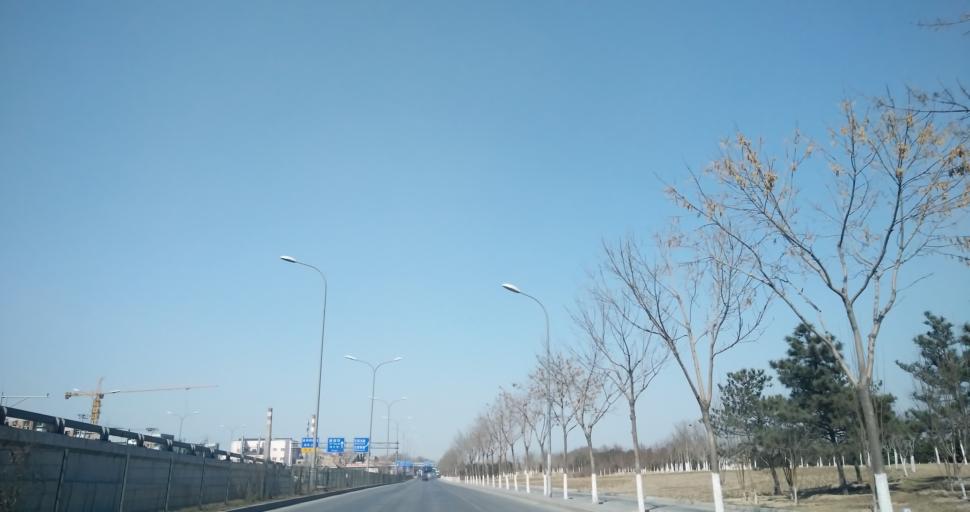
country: CN
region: Beijing
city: Jiugong
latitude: 39.7897
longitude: 116.4245
